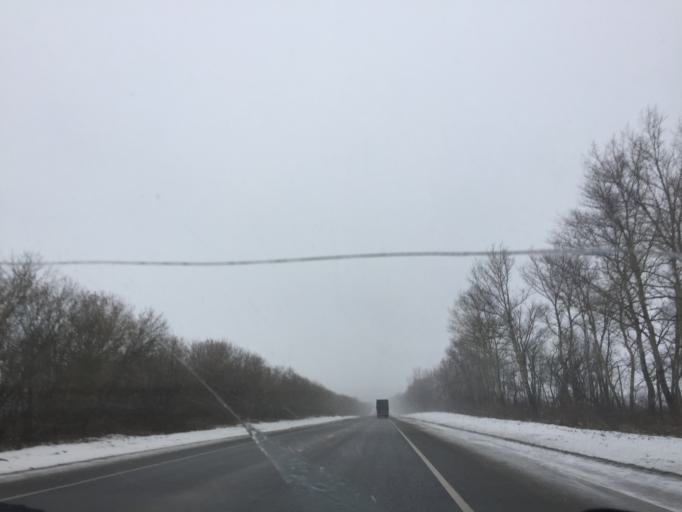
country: RU
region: Tula
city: Plavsk
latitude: 53.7699
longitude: 37.3476
